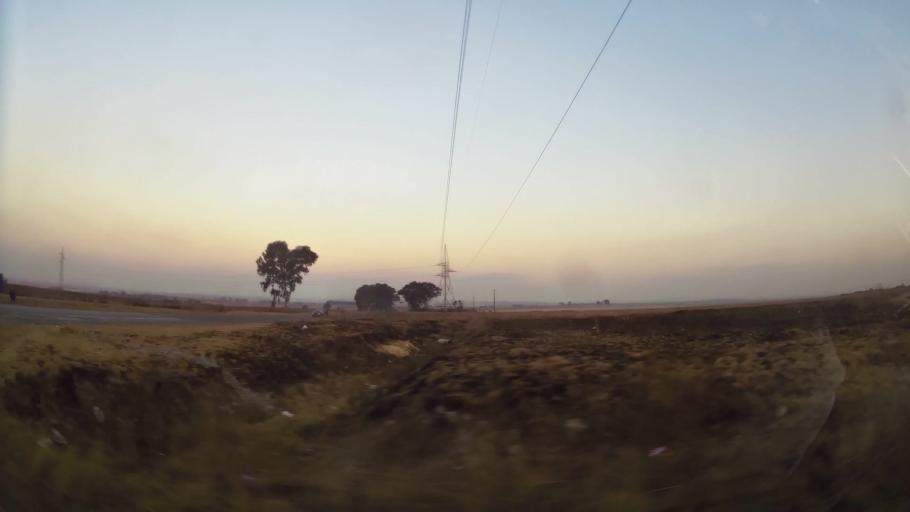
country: ZA
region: Gauteng
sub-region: Ekurhuleni Metropolitan Municipality
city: Nigel
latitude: -26.3800
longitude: 28.4223
